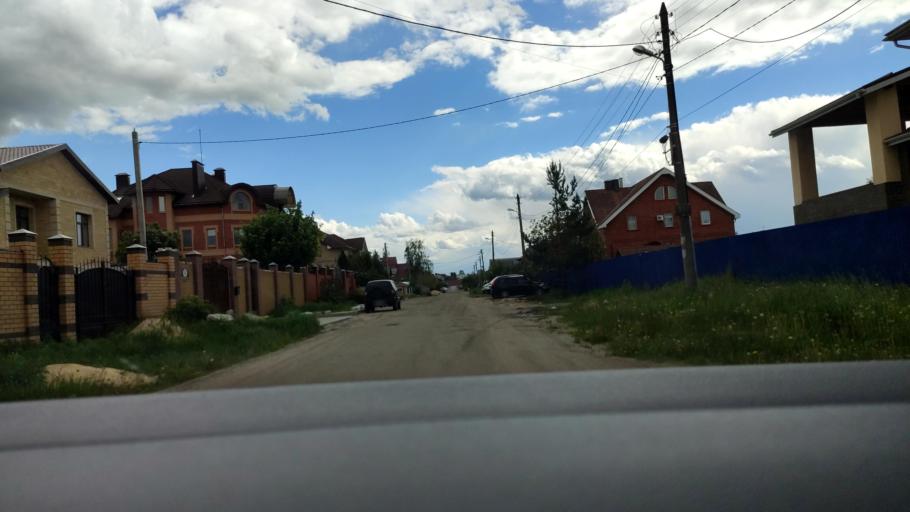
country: RU
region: Voronezj
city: Somovo
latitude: 51.6865
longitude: 39.3063
